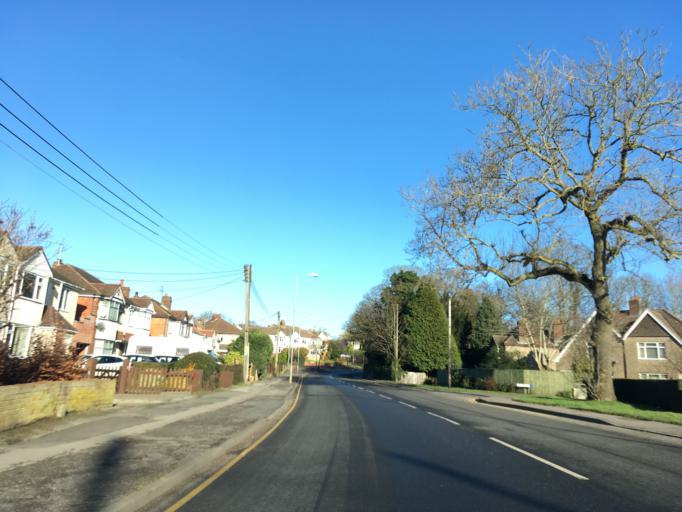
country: GB
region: England
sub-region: Wiltshire
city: Chippenham
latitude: 51.4670
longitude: -2.1140
